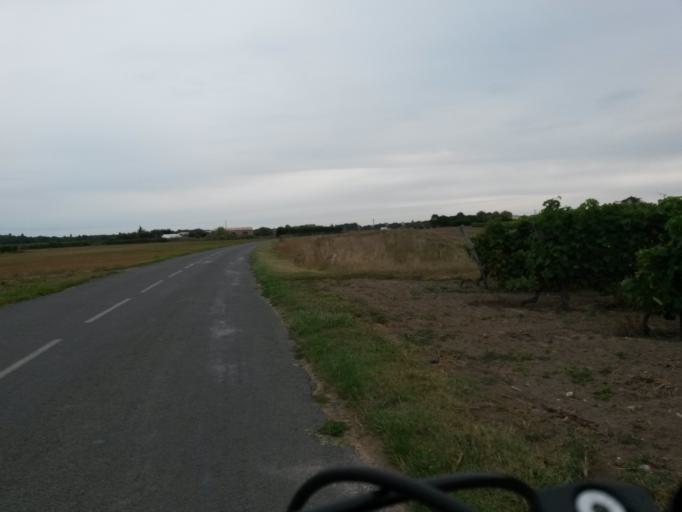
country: FR
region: Poitou-Charentes
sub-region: Departement de la Charente-Maritime
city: Dolus-d'Oleron
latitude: 45.9389
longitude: -1.3423
